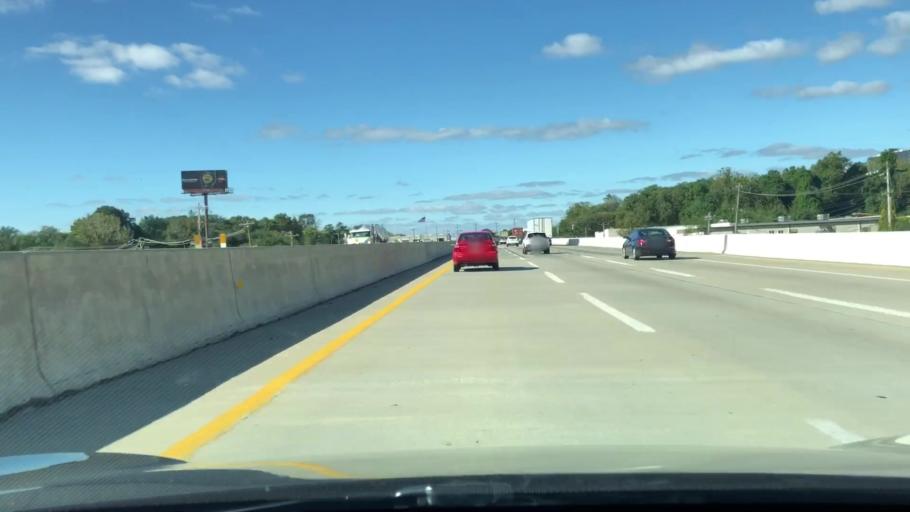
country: US
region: Pennsylvania
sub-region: Montgomery County
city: Bridgeport
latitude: 40.0878
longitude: -75.3562
